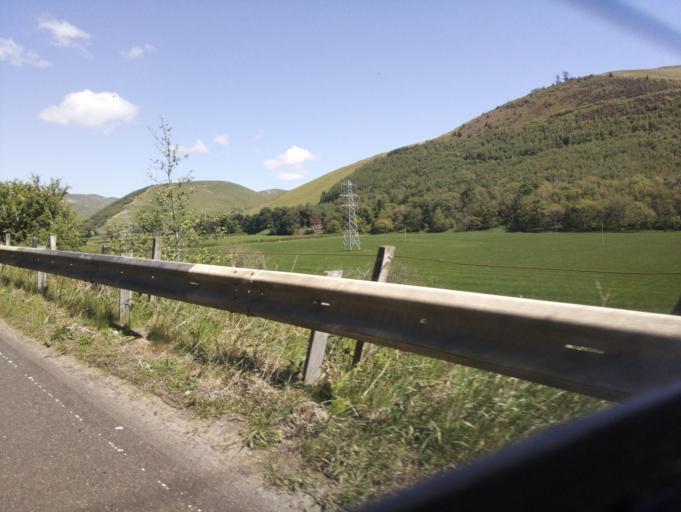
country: GB
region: Scotland
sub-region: Dumfries and Galloway
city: Langholm
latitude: 55.2365
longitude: -2.9747
